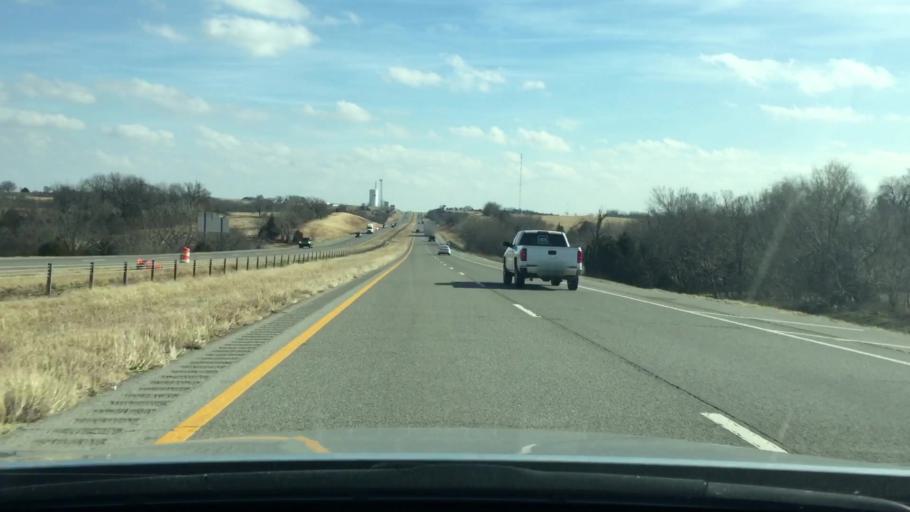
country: US
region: Oklahoma
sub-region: Cleveland County
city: Noble
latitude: 35.0762
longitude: -97.4049
